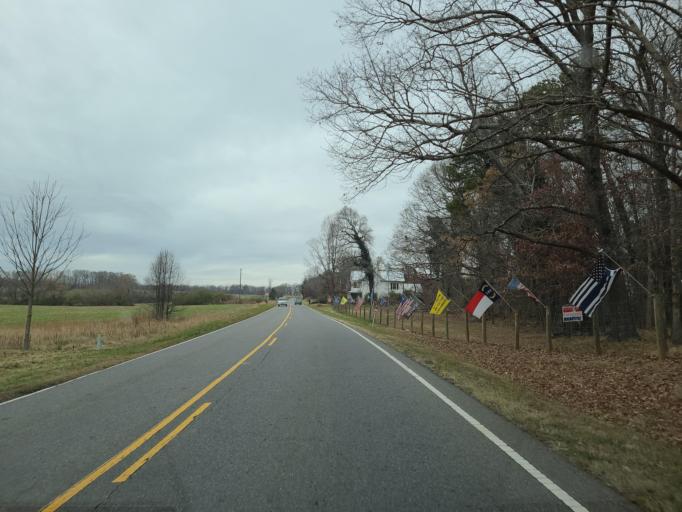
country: US
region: North Carolina
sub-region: Cleveland County
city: Shelby
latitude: 35.3650
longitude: -81.5779
